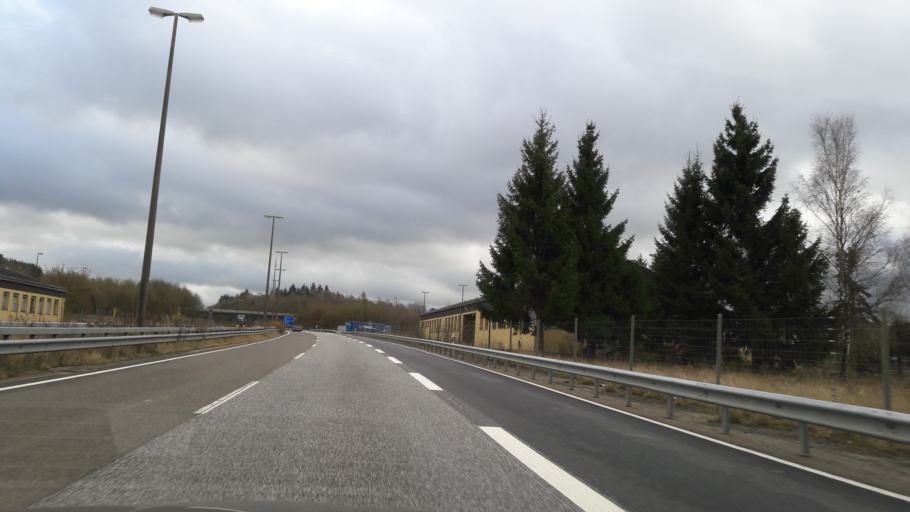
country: DE
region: Rheinland-Pfalz
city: Winterspelt
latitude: 50.2308
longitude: 6.1860
